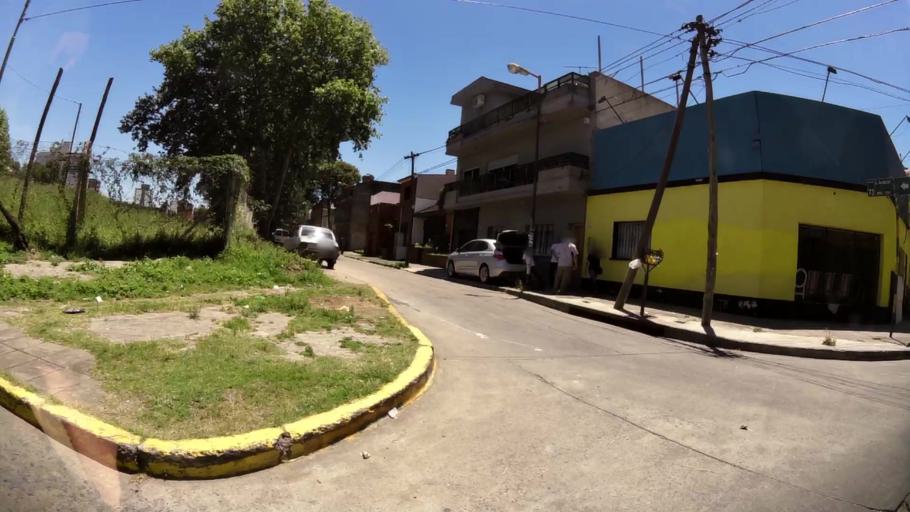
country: AR
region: Buenos Aires
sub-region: Partido de General San Martin
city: General San Martin
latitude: -34.5756
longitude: -58.5288
